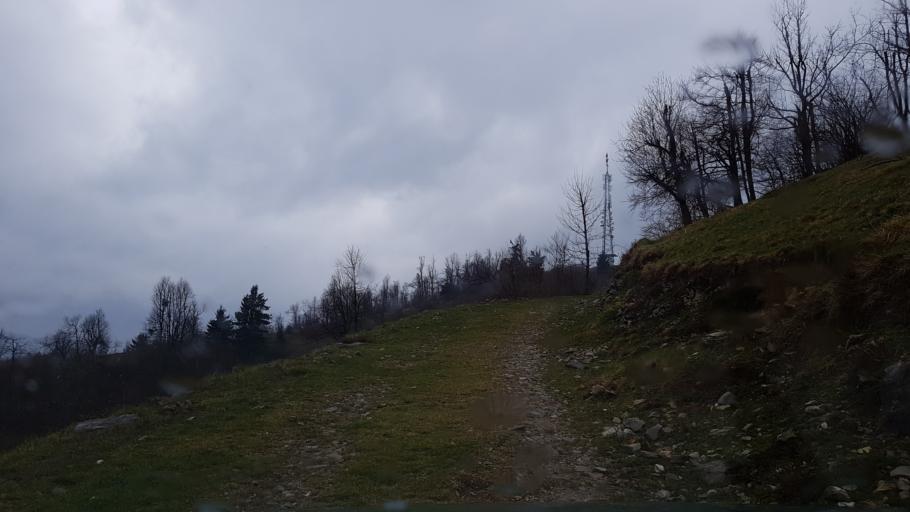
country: SI
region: Cerkno
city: Cerkno
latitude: 46.1421
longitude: 13.8683
